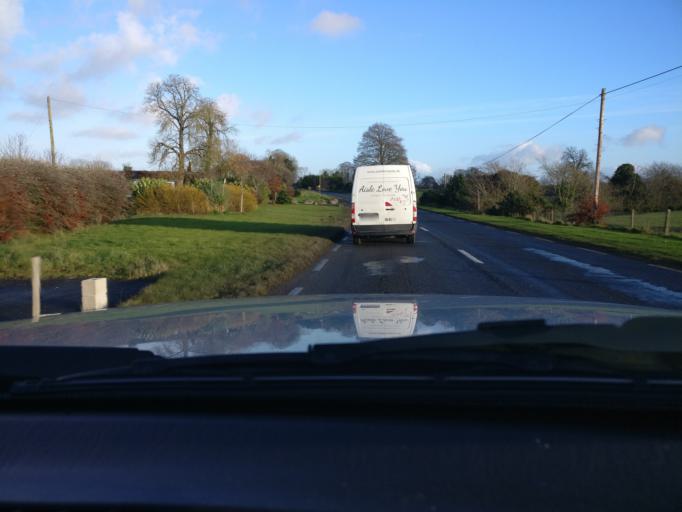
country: IE
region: Leinster
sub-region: An Mhi
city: Kells
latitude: 53.7212
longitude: -6.9625
